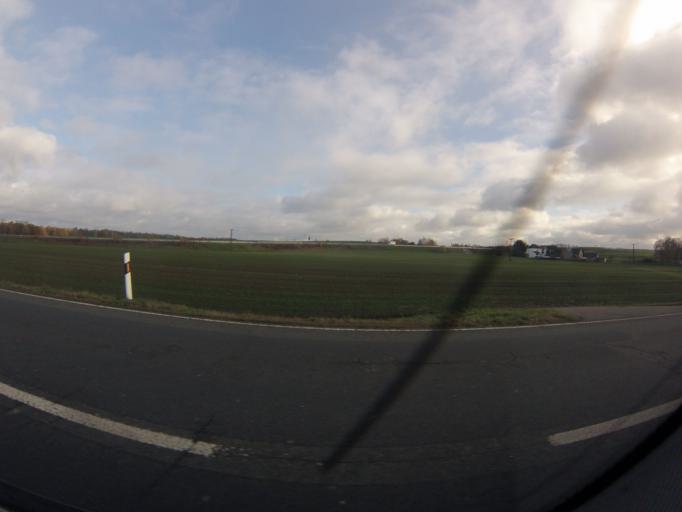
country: DE
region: Thuringia
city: Gossnitz
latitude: 50.9136
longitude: 12.4432
